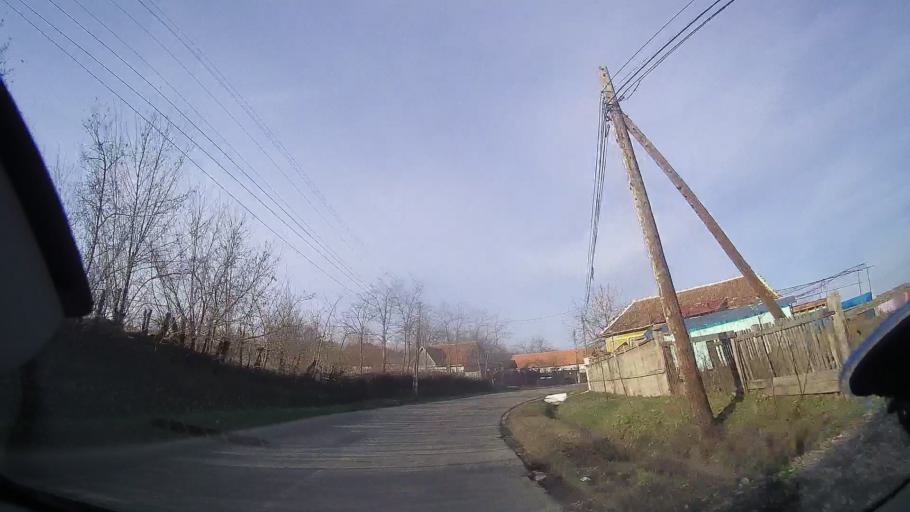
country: RO
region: Bihor
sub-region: Comuna Brusturi
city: Brusturi
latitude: 47.1660
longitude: 22.2210
